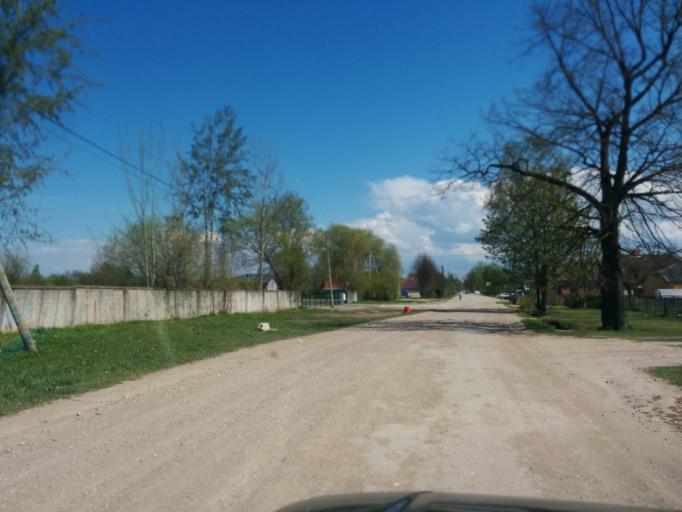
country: LV
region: Jelgava
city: Jelgava
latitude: 56.6301
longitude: 23.7168
